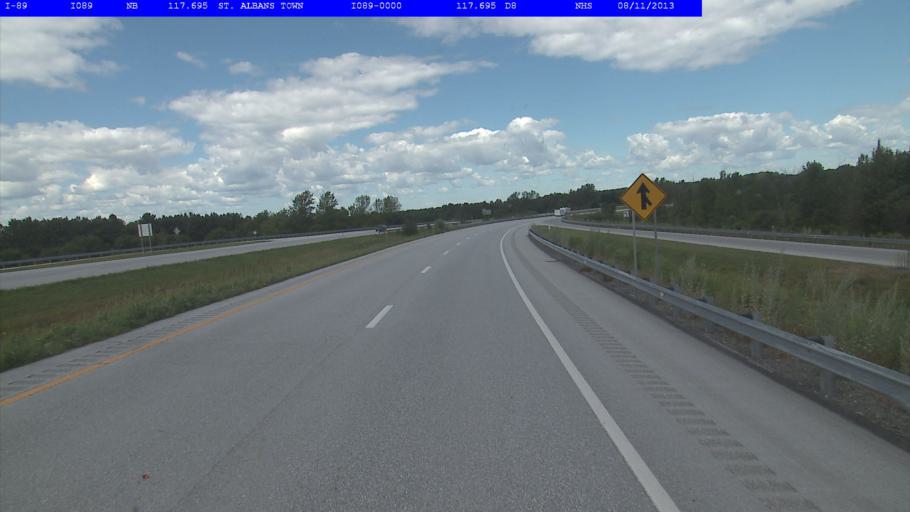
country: US
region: Vermont
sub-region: Franklin County
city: Saint Albans
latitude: 44.8446
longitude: -73.0807
